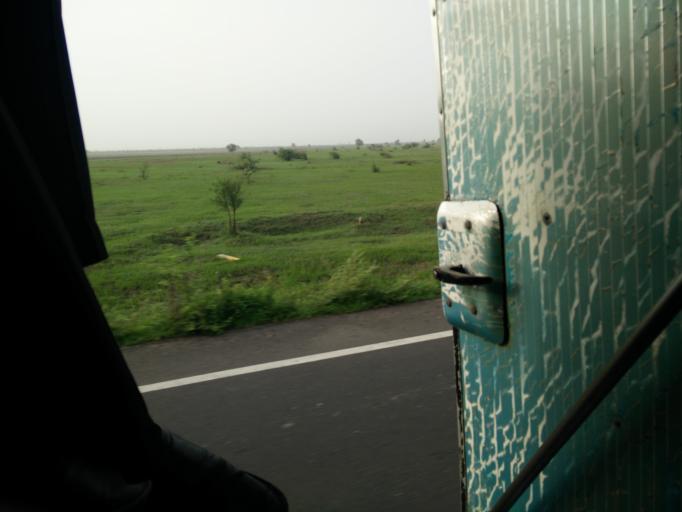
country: IN
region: Gujarat
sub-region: Ahmadabad
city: Dholka
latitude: 22.7134
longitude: 72.2569
